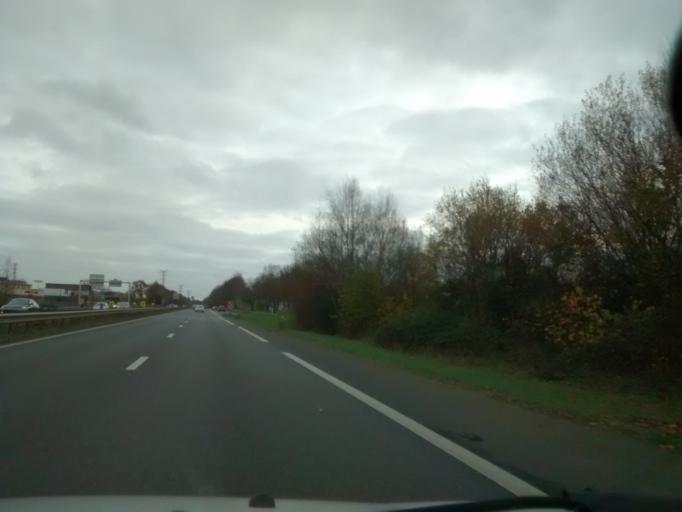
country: FR
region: Brittany
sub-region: Departement d'Ille-et-Vilaine
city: La Meziere
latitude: 48.2039
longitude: -1.7340
